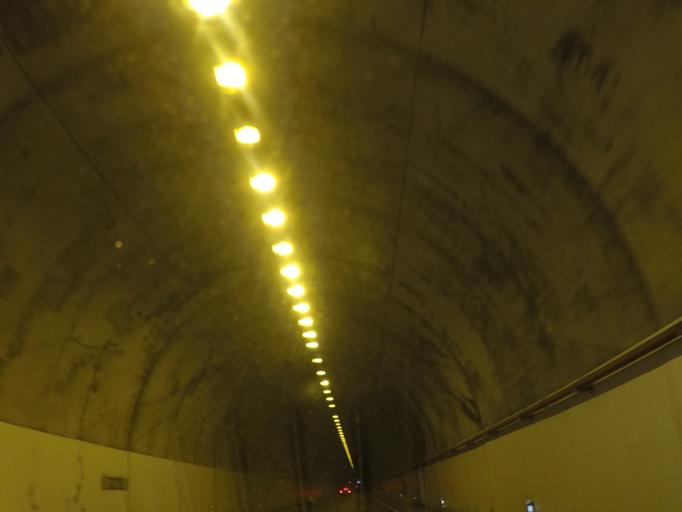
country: PT
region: Madeira
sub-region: Ribeira Brava
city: Campanario
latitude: 32.6695
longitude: -17.0423
